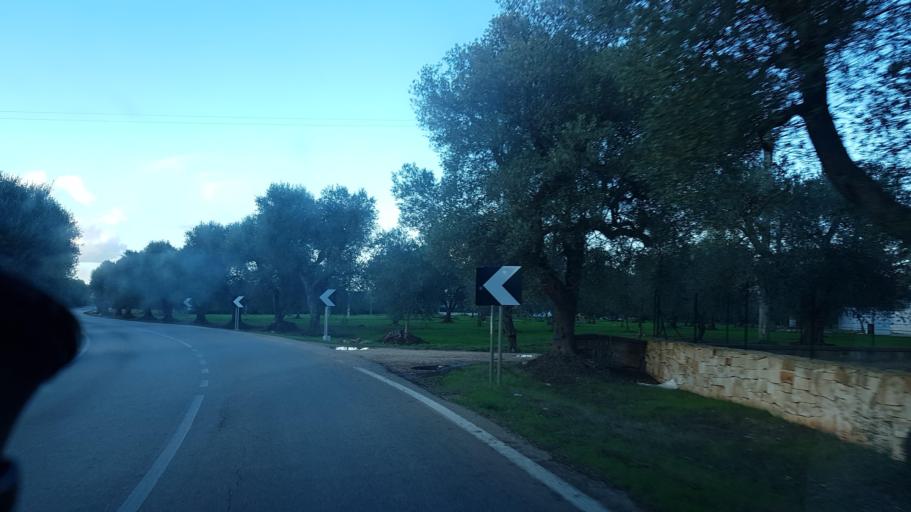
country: IT
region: Apulia
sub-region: Provincia di Brindisi
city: San Michele Salentino
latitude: 40.6542
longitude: 17.6044
